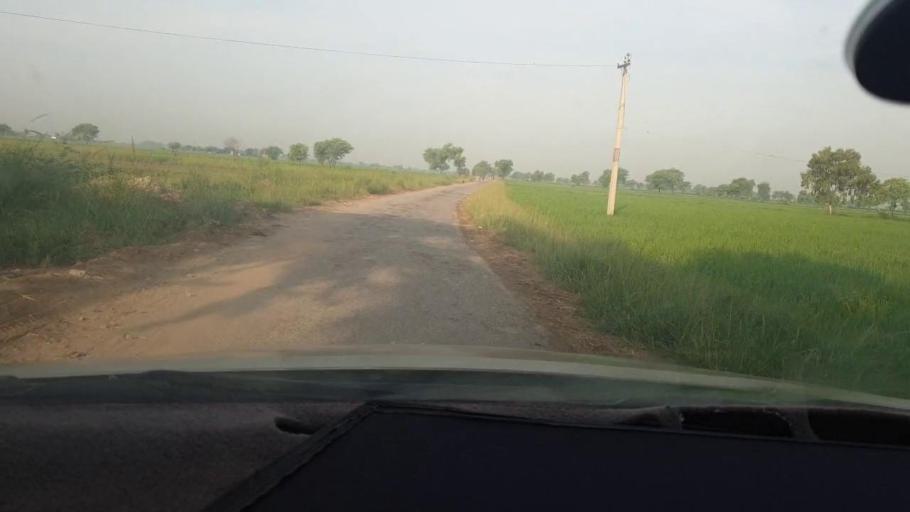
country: PK
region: Sindh
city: Jacobabad
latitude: 28.3013
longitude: 68.4255
